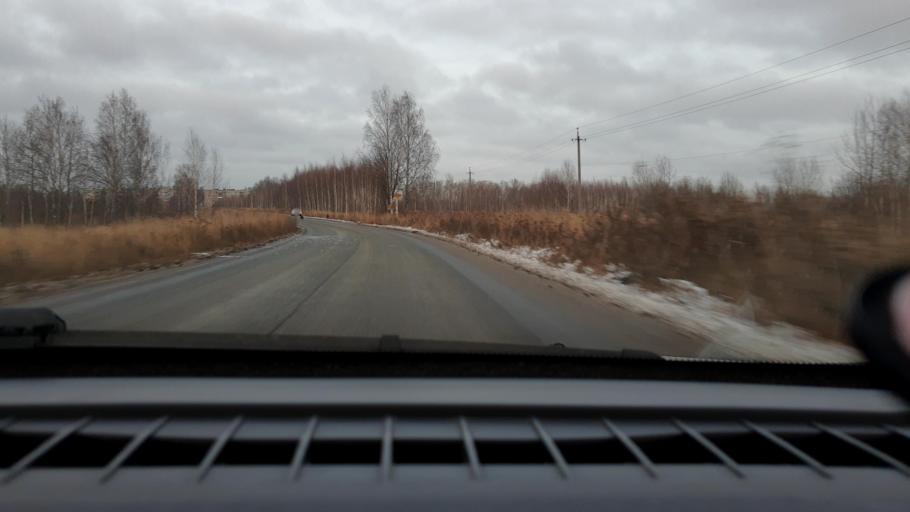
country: RU
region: Nizjnij Novgorod
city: Gorbatovka
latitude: 56.2387
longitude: 43.7418
